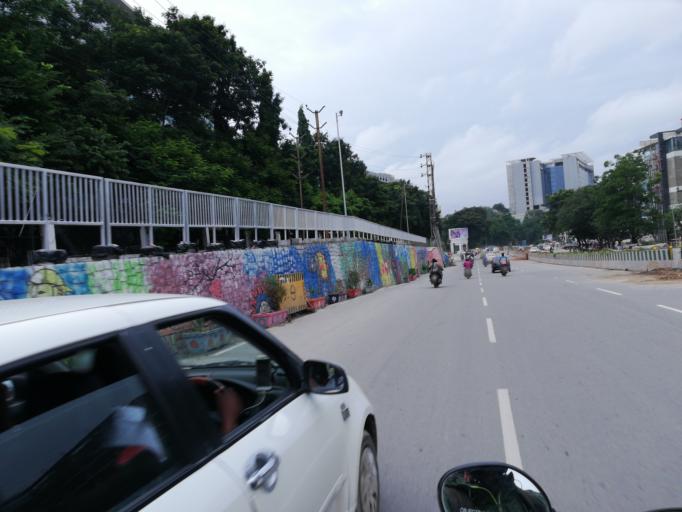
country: IN
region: Telangana
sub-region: Rangareddi
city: Kukatpalli
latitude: 17.4446
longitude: 78.3771
